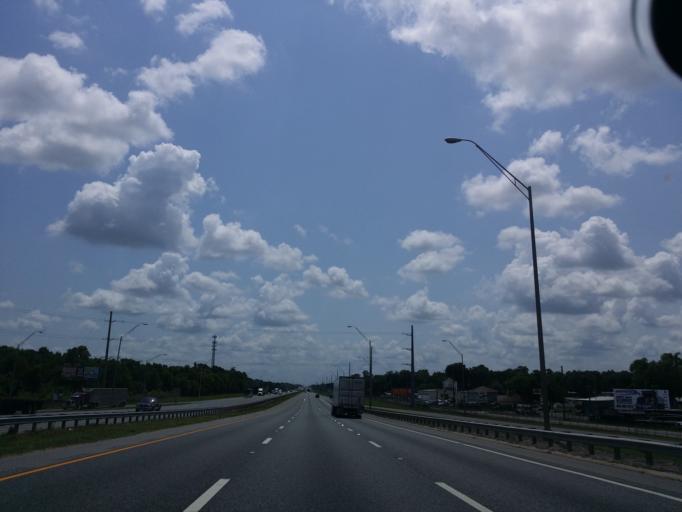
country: US
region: Florida
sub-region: Marion County
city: Ocala
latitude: 29.2049
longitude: -82.1847
